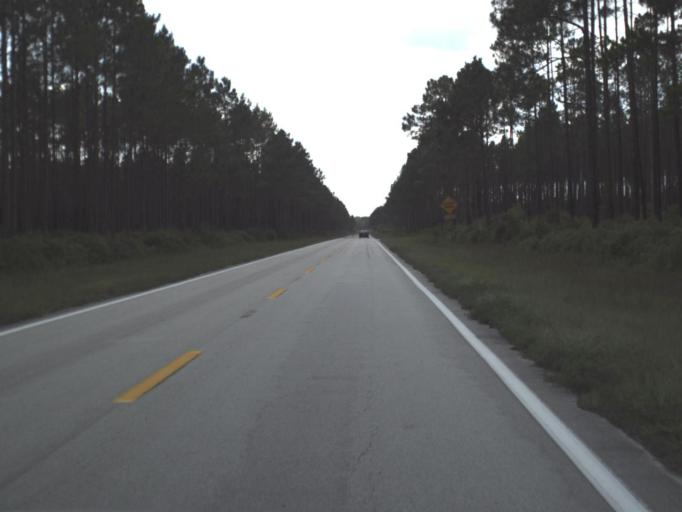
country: US
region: Florida
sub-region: Baker County
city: Macclenny
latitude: 30.5598
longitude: -82.3826
